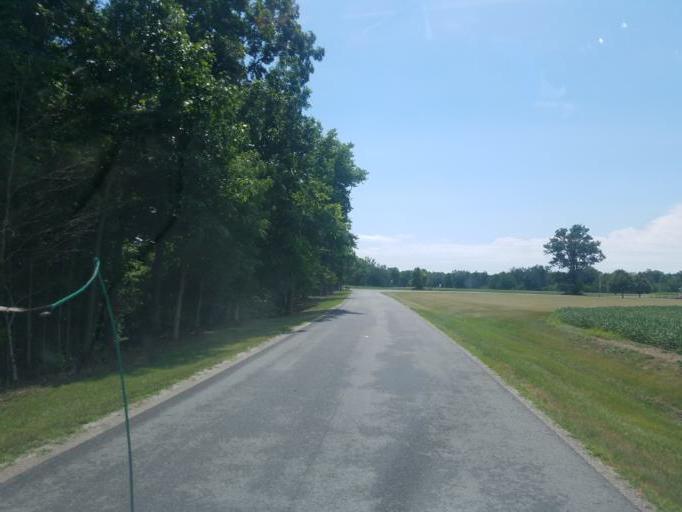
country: US
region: Ohio
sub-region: Paulding County
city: Antwerp
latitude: 41.1798
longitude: -84.7893
